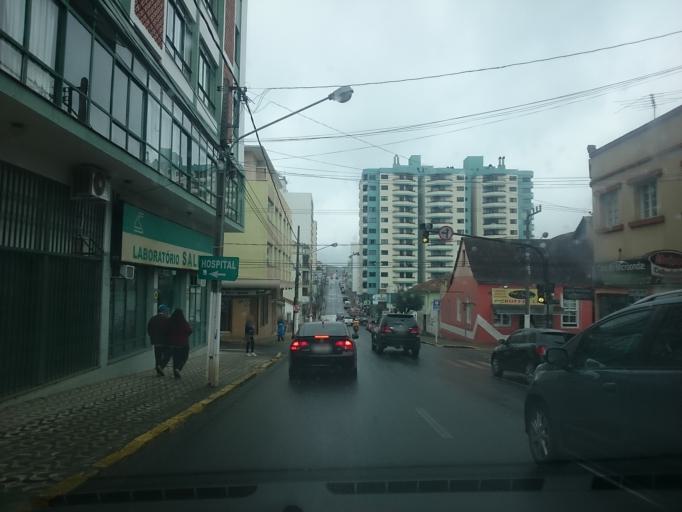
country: BR
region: Santa Catarina
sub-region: Lages
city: Lages
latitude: -27.8174
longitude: -50.3288
